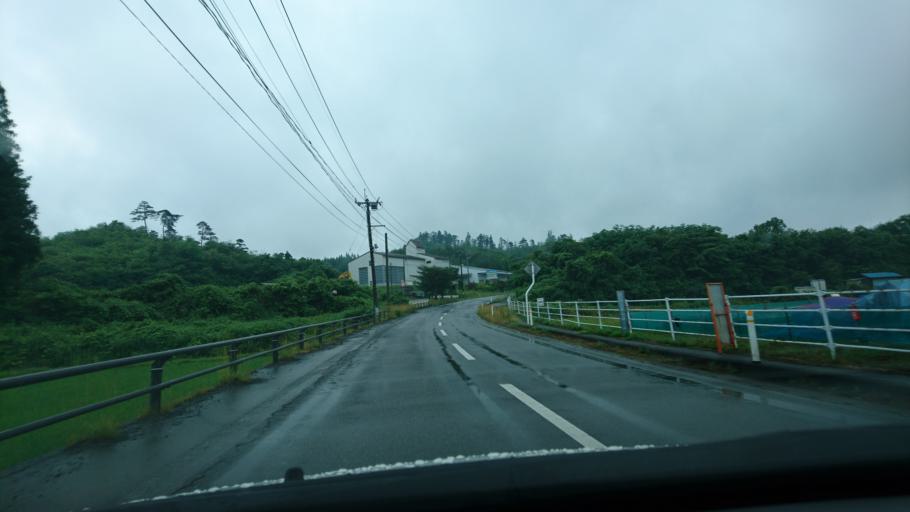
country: JP
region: Iwate
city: Ichinoseki
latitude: 38.9383
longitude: 141.0626
